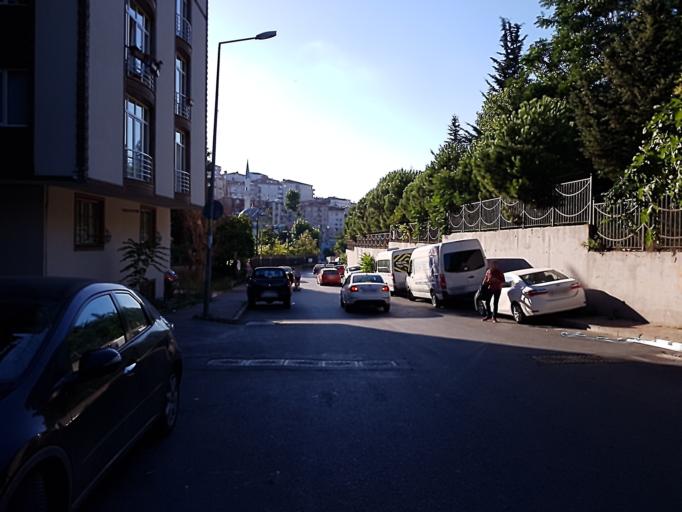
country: TR
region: Istanbul
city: Sisli
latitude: 41.0721
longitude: 29.0036
